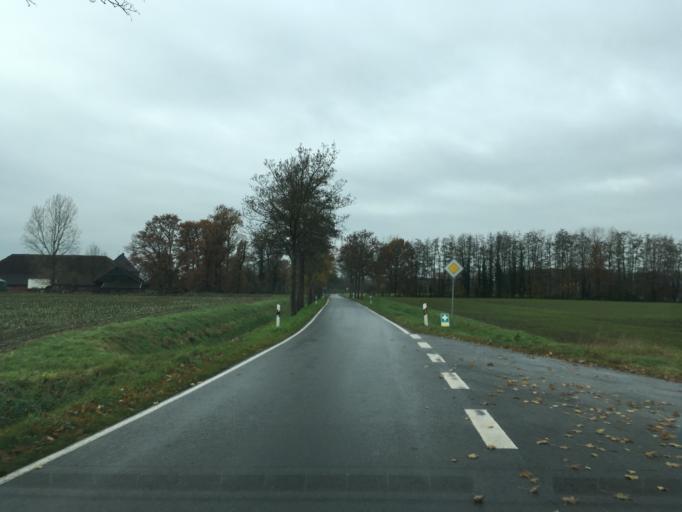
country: DE
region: North Rhine-Westphalia
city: Stadtlohn
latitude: 52.0110
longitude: 6.9586
